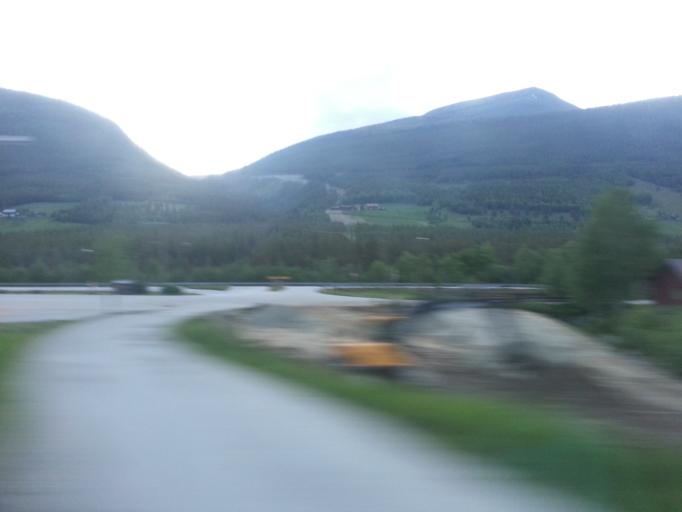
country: NO
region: Oppland
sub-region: Dovre
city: Dovre
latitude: 61.9203
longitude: 9.3348
